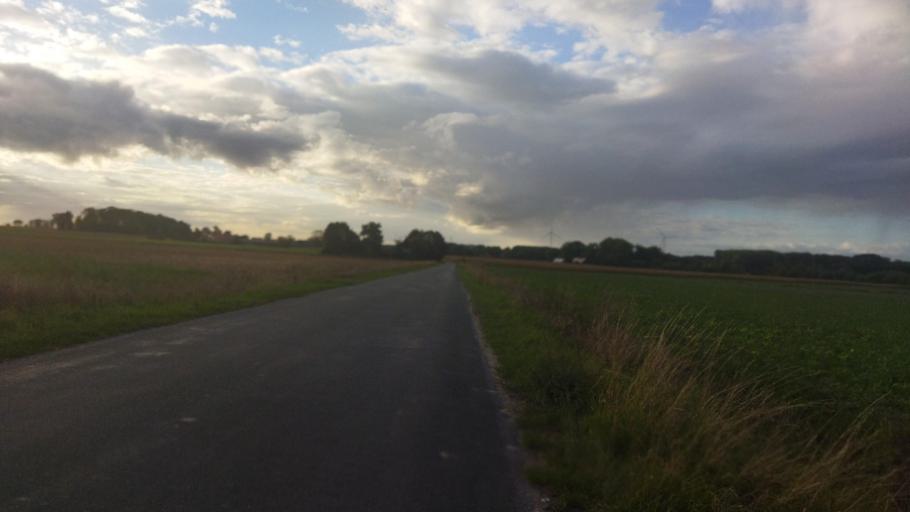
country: DE
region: North Rhine-Westphalia
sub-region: Regierungsbezirk Munster
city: Billerbeck
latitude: 51.9747
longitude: 7.2428
